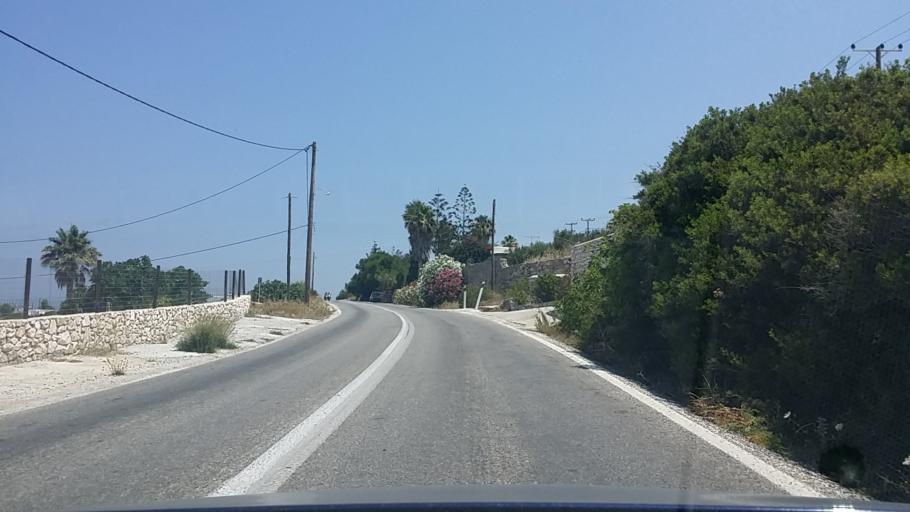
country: GR
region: South Aegean
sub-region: Nomos Kykladon
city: Paros
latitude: 37.0603
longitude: 25.1190
